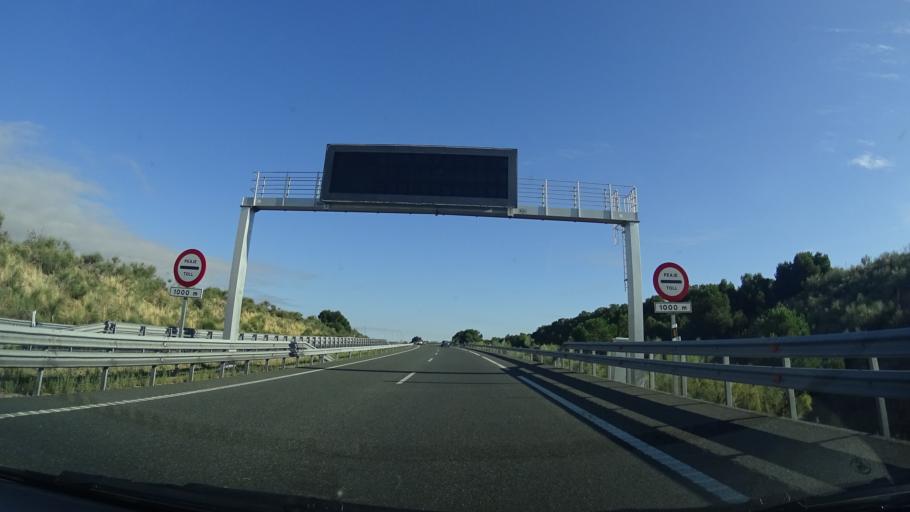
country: ES
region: Castille and Leon
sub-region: Provincia de Avila
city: Sanchidrian
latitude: 40.8751
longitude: -4.5671
